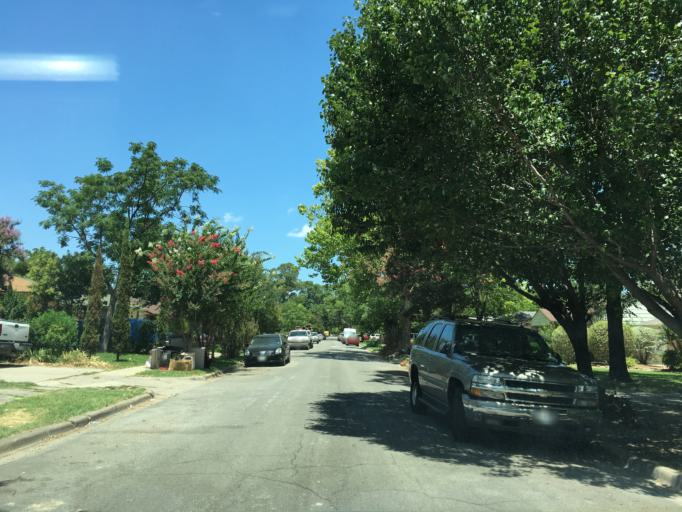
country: US
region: Texas
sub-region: Dallas County
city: Garland
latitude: 32.8466
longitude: -96.6699
